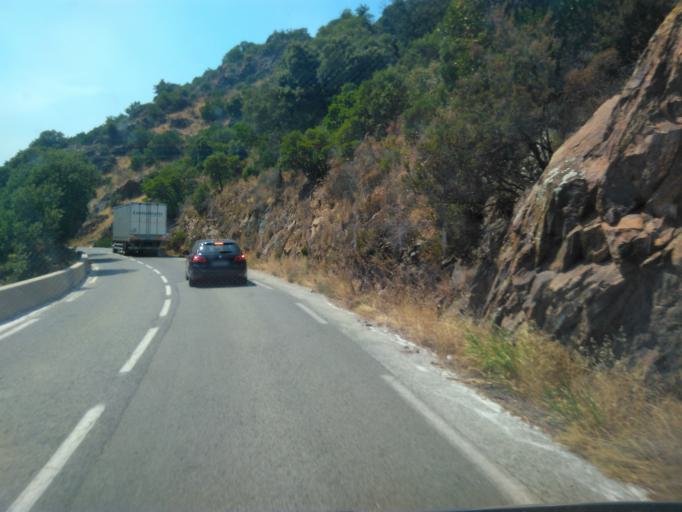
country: FR
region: Provence-Alpes-Cote d'Azur
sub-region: Departement du Var
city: La Garde-Freinet
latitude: 43.3316
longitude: 6.4529
